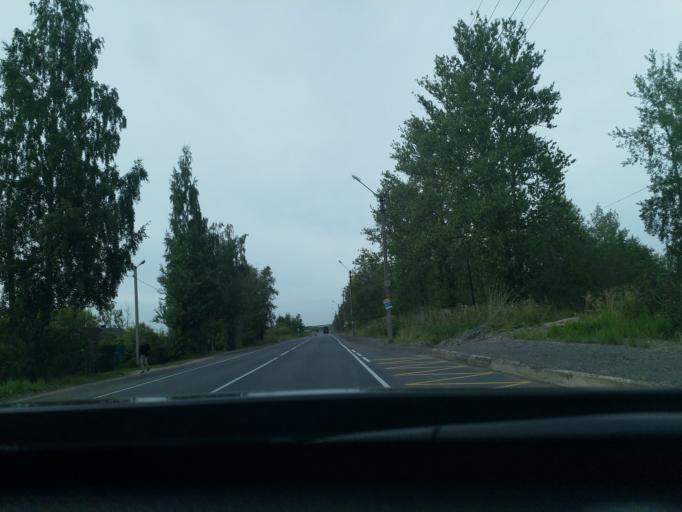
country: RU
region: Leningrad
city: Nikol'skoye
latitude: 59.7164
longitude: 30.7791
